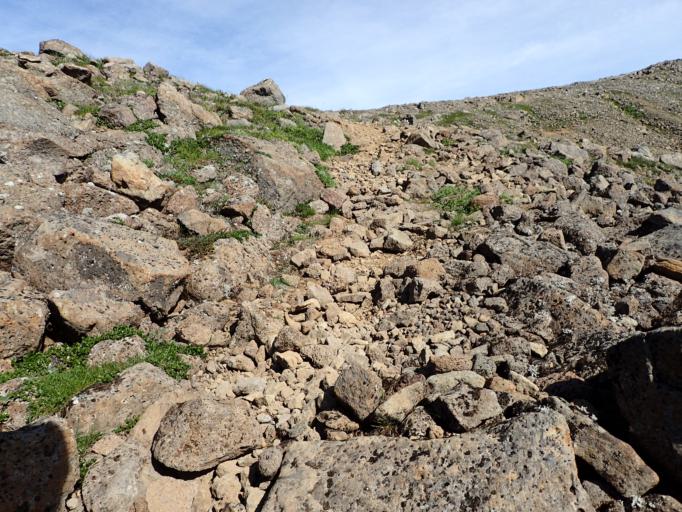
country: IS
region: West
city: Olafsvik
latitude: 65.6388
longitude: -23.7755
